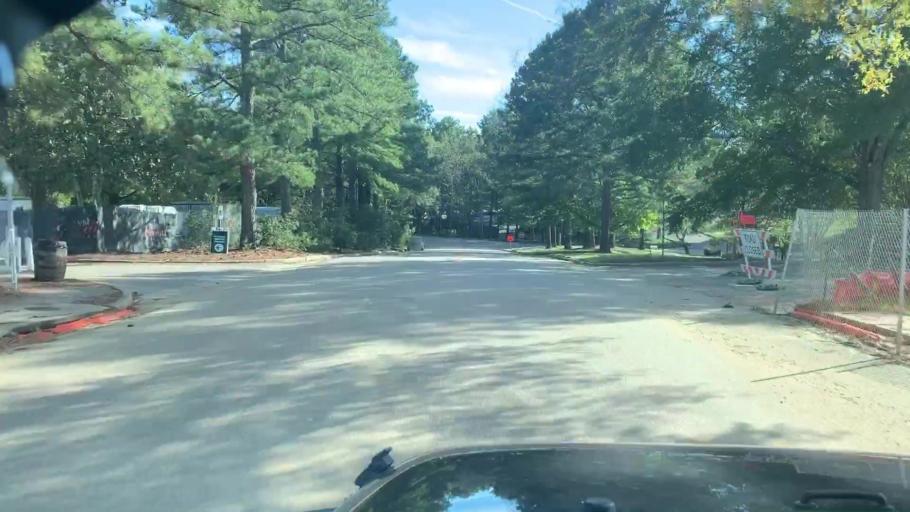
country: US
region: Virginia
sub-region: City of Williamsburg
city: Williamsburg
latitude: 37.2679
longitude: -76.7037
